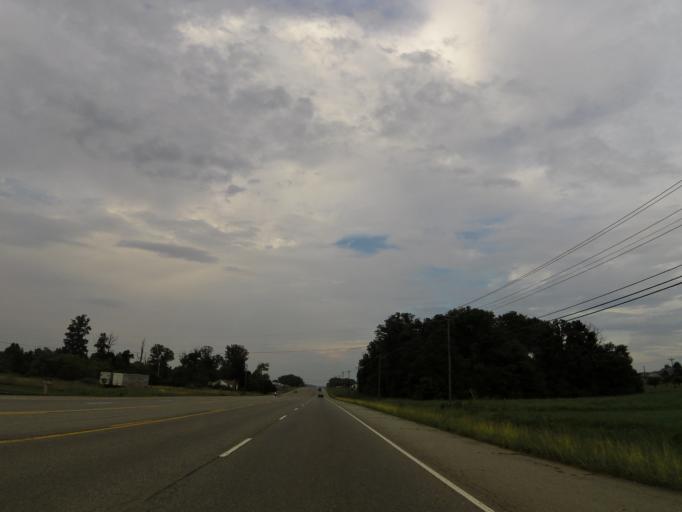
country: US
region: Tennessee
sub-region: Loudon County
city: Greenback
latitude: 35.6524
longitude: -84.1280
